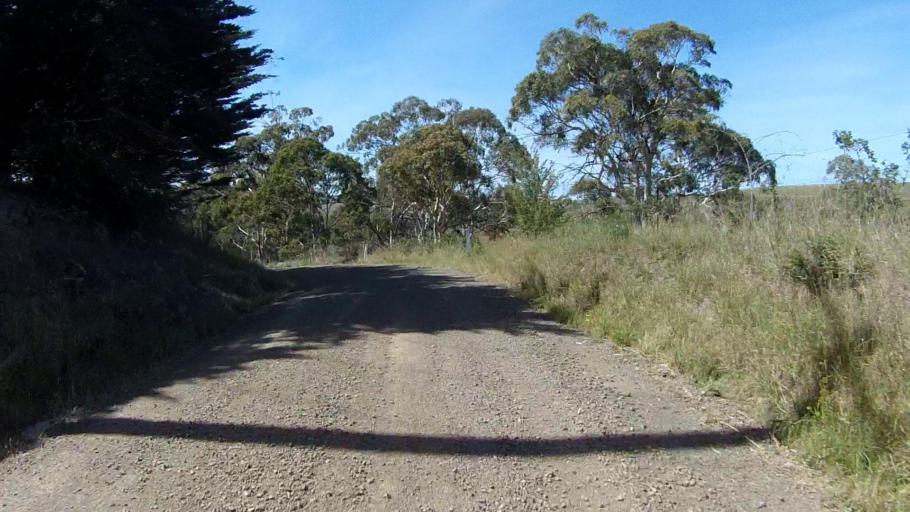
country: AU
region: Tasmania
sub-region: Sorell
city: Sorell
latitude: -42.7466
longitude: 147.6114
